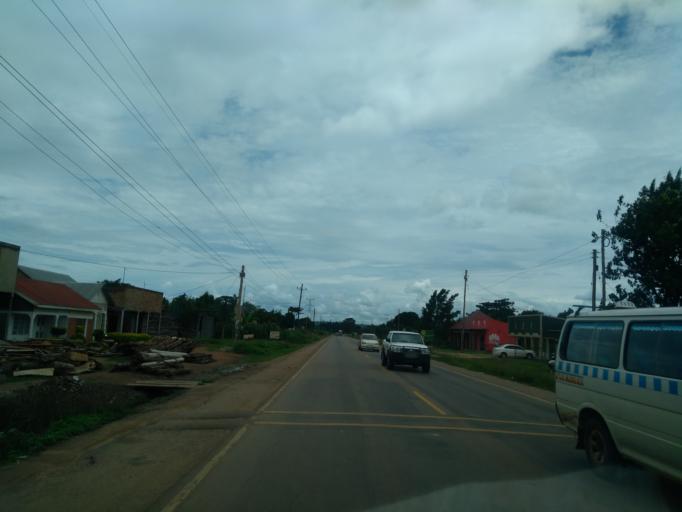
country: UG
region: Central Region
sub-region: Butambala District
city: Gombe
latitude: -0.0168
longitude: 32.0283
